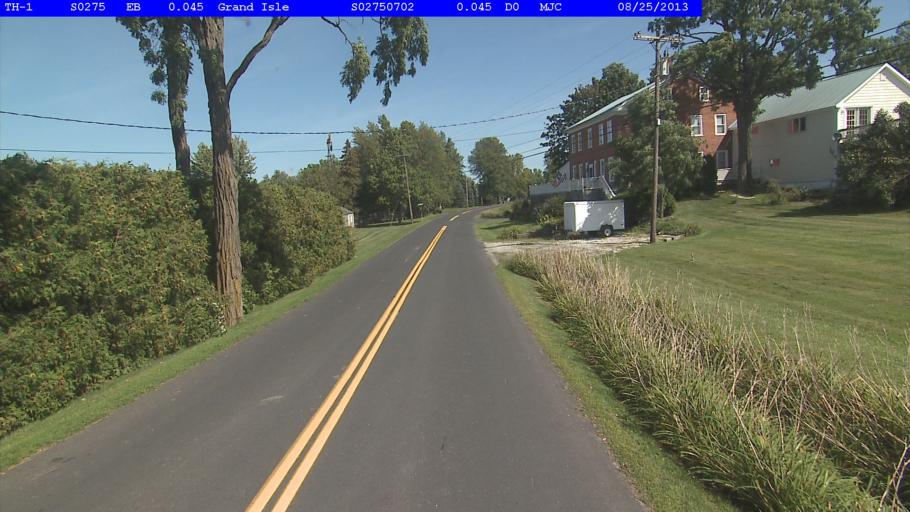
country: US
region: New York
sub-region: Clinton County
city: Cumberland Head
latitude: 44.7019
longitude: -73.3475
